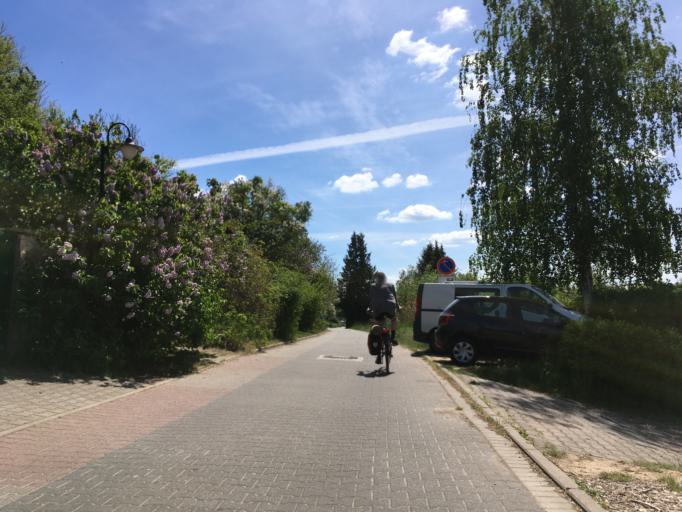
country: DE
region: Brandenburg
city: Niederfinow
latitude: 52.8426
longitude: 13.8990
